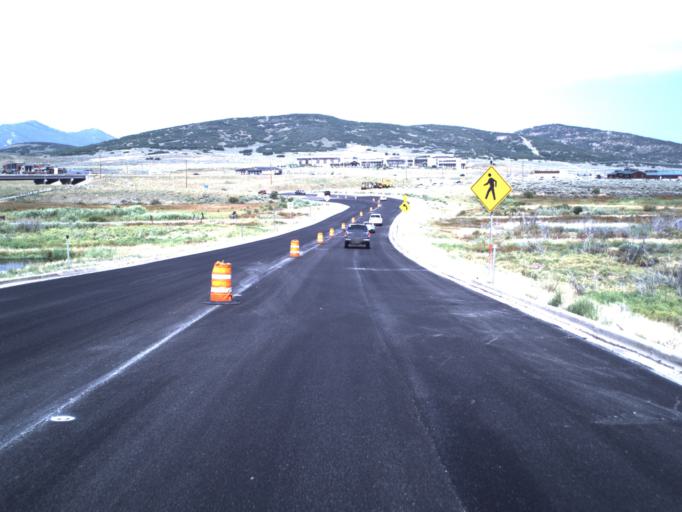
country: US
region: Utah
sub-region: Summit County
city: Park City
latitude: 40.6828
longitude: -111.4556
